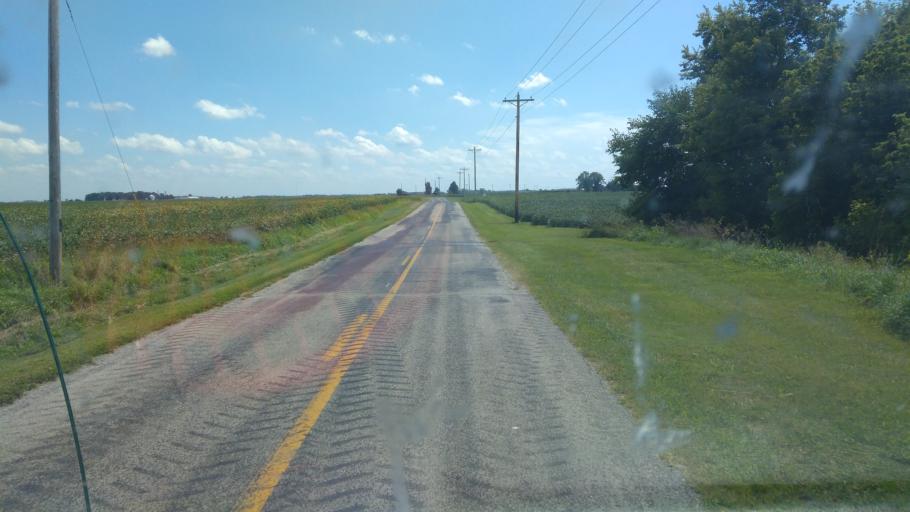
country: US
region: Ohio
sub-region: Wyandot County
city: Upper Sandusky
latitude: 40.6719
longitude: -83.2953
